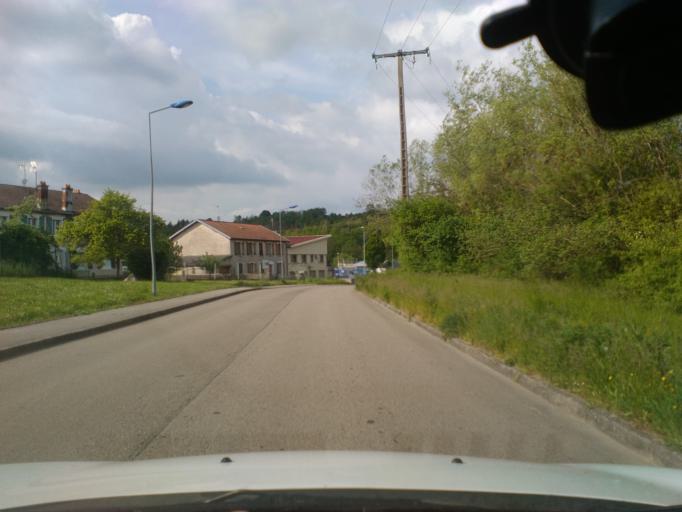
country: FR
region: Lorraine
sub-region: Departement des Vosges
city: Mirecourt
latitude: 48.3105
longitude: 6.1349
